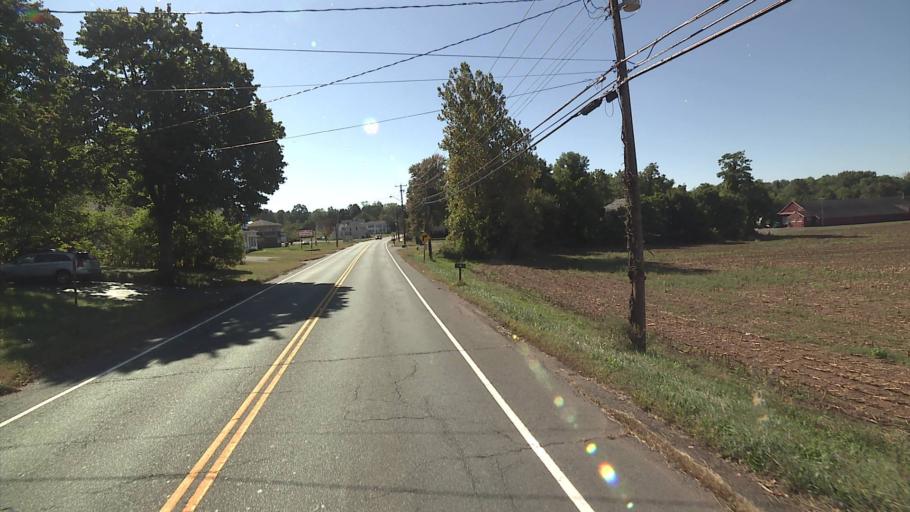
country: US
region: Connecticut
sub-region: Tolland County
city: Rockville
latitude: 41.8749
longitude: -72.4635
